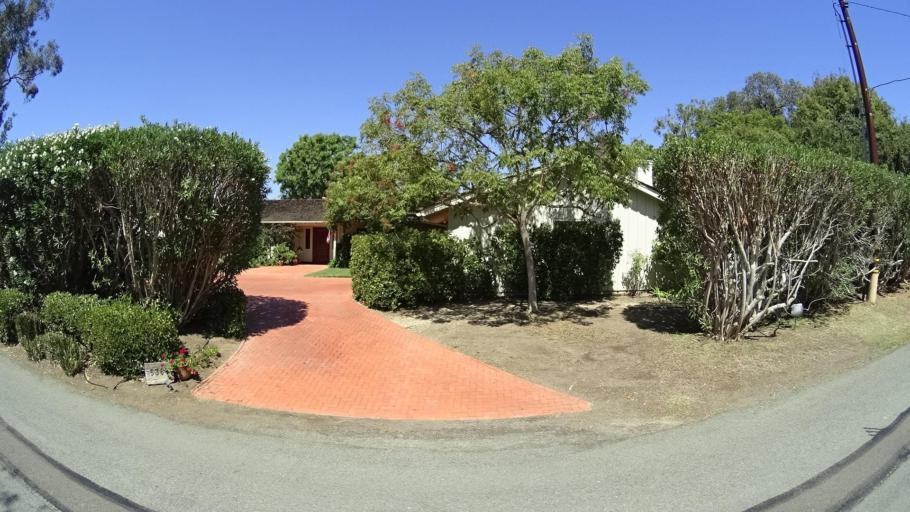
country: US
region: California
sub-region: San Diego County
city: Rancho Santa Fe
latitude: 33.0144
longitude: -117.2158
